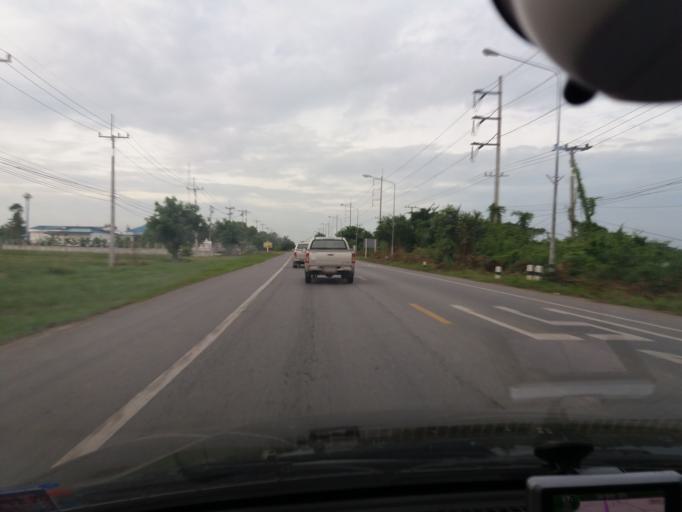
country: TH
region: Suphan Buri
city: U Thong
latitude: 14.5085
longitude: 99.9165
